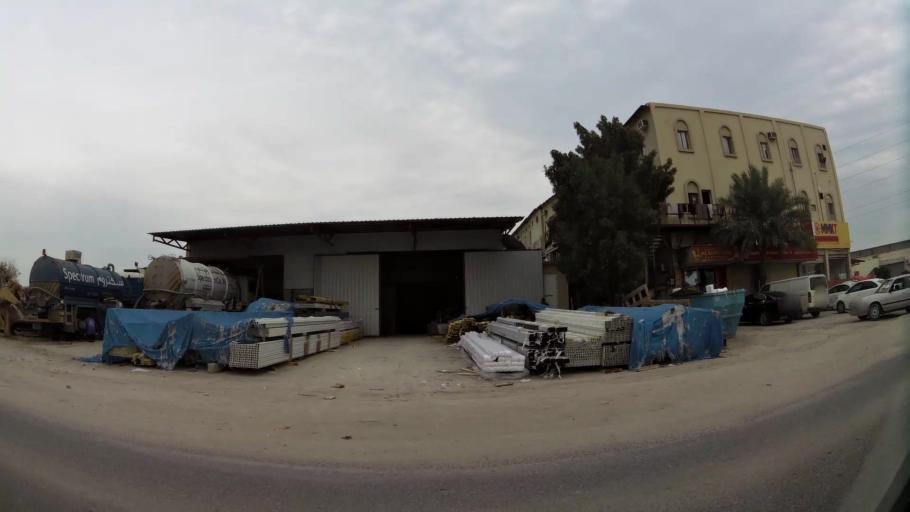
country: BH
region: Northern
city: Sitrah
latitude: 26.1372
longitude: 50.6064
